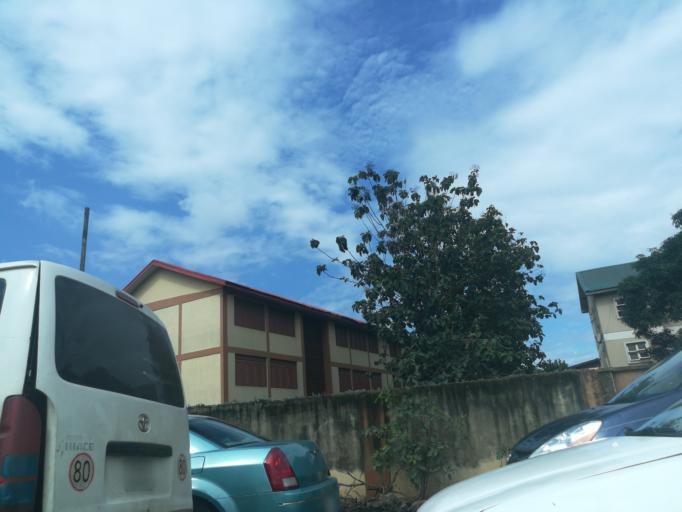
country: NG
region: Lagos
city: Agege
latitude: 6.6249
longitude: 3.3267
